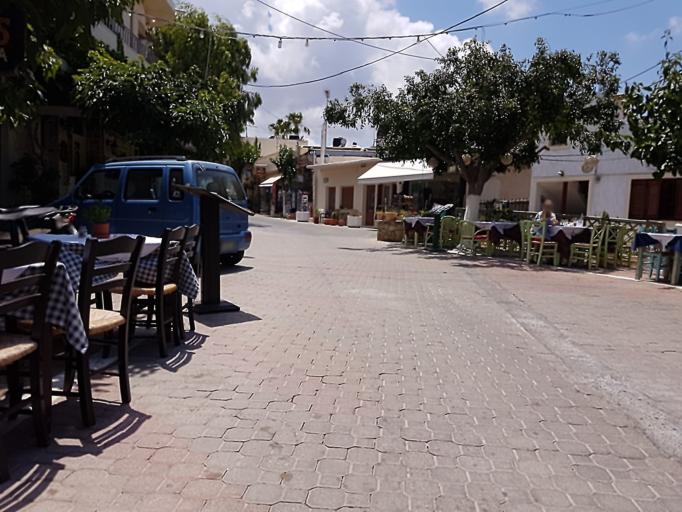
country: GR
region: Crete
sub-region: Nomos Irakleiou
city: Limin Khersonisou
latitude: 35.3081
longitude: 25.3721
